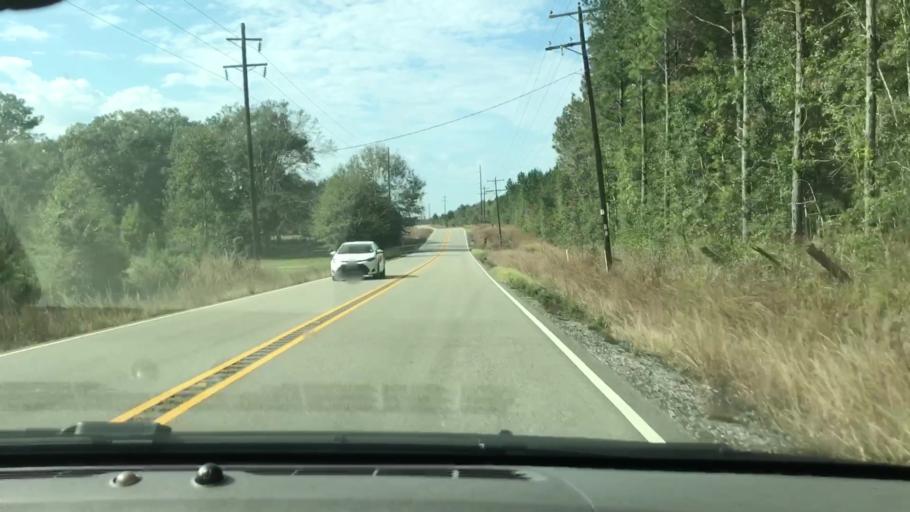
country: US
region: Louisiana
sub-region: Saint Tammany Parish
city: Abita Springs
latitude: 30.5266
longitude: -89.9204
